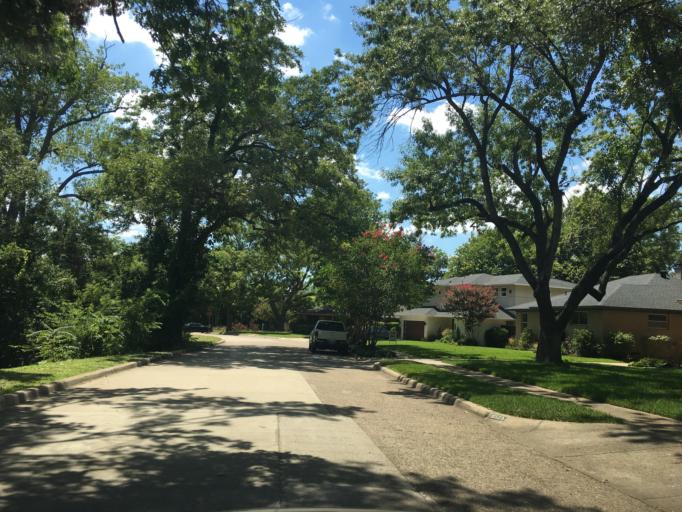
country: US
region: Texas
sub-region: Dallas County
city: Garland
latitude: 32.8514
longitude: -96.6987
